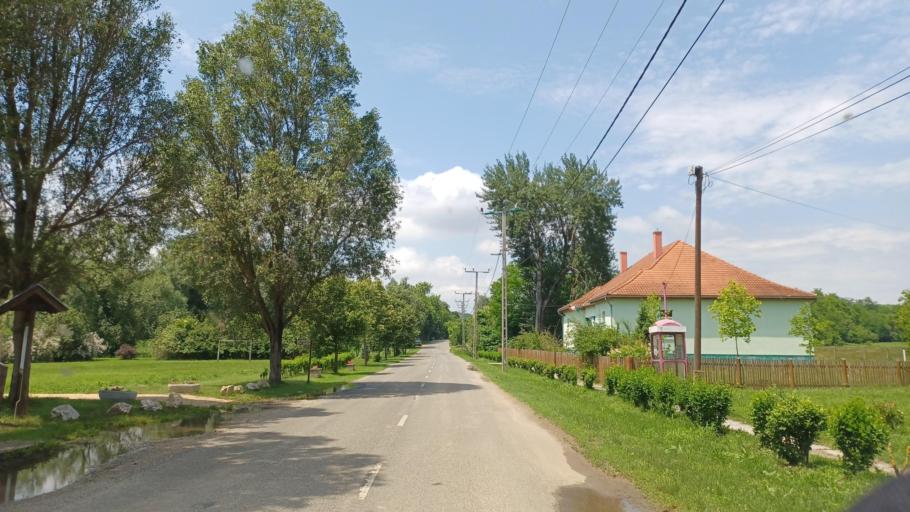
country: HU
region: Tolna
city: Simontornya
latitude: 46.6796
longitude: 18.5347
